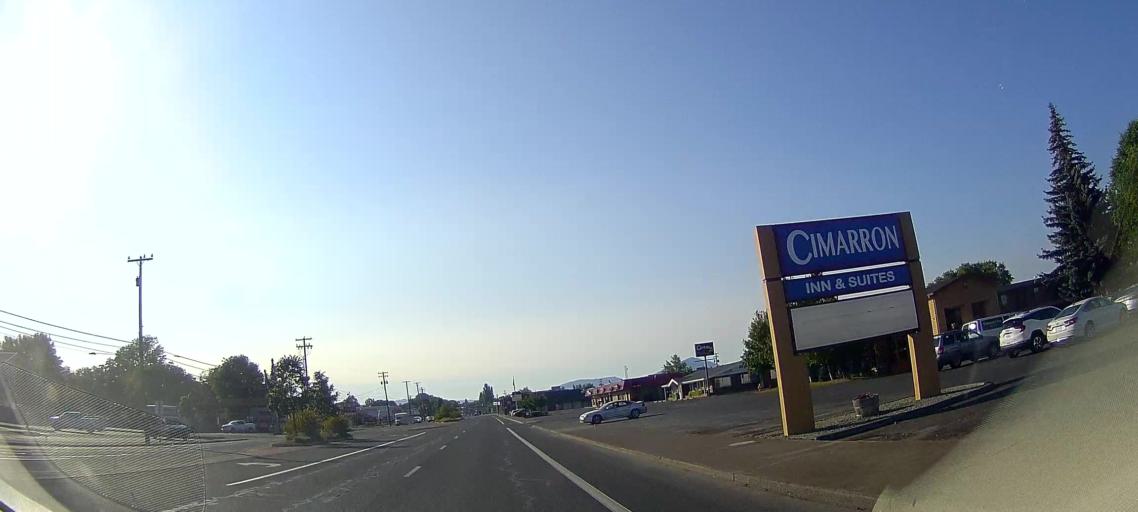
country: US
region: Oregon
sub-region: Klamath County
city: Altamont
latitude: 42.2084
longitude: -121.7516
